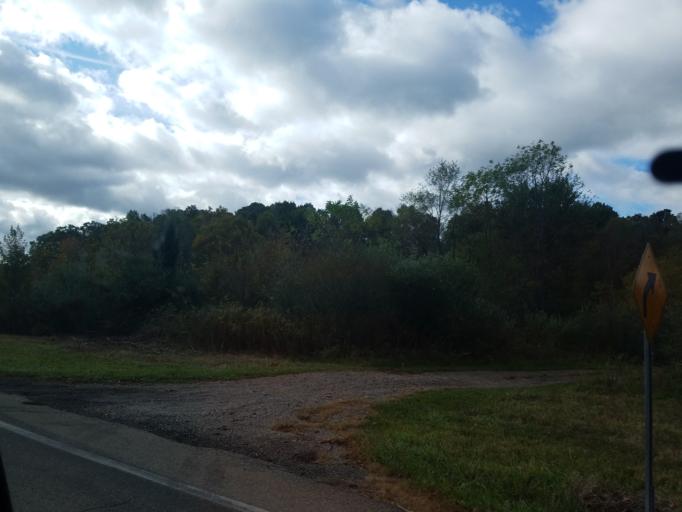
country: US
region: Ohio
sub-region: Vinton County
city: McArthur
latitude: 39.1890
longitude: -82.4679
